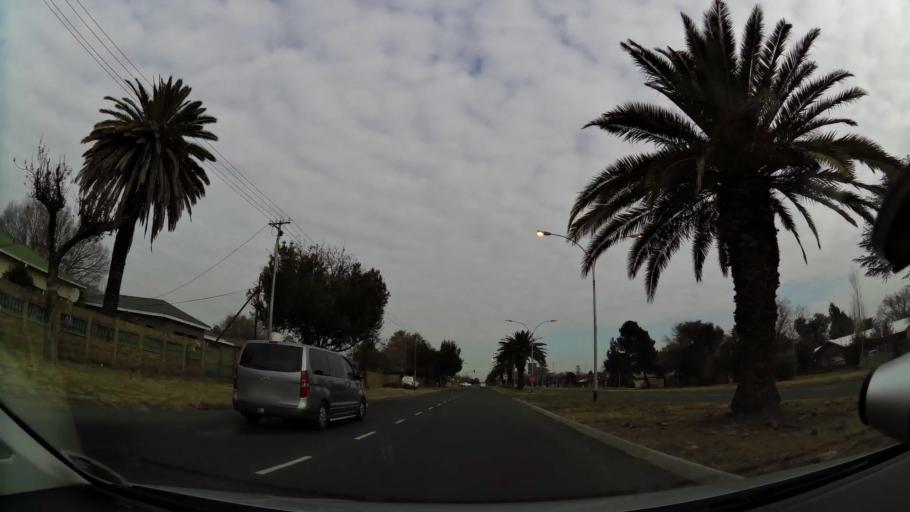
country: ZA
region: Orange Free State
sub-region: Mangaung Metropolitan Municipality
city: Bloemfontein
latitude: -29.1264
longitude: 26.1793
